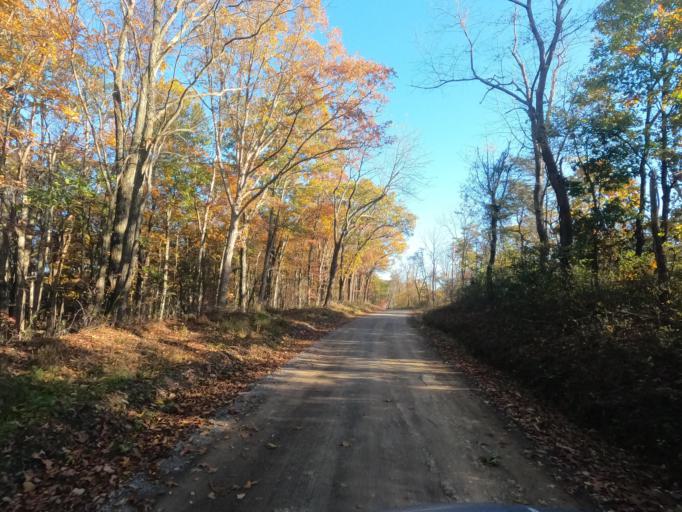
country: US
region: West Virginia
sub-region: Mineral County
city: Fort Ashby
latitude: 39.5605
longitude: -78.5240
